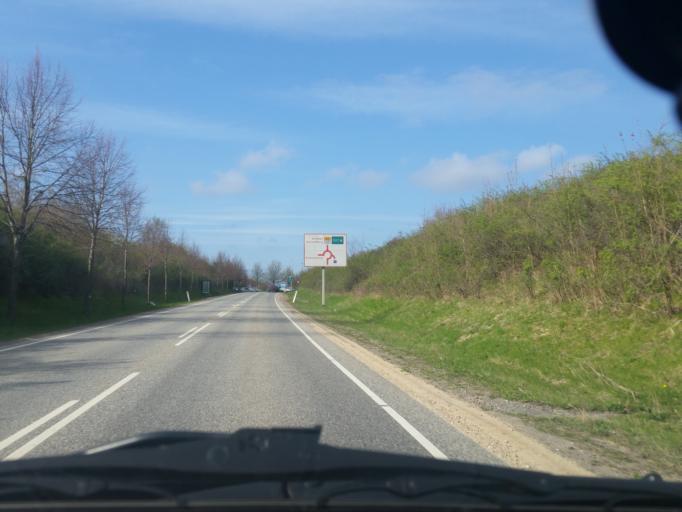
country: DK
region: Zealand
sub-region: Soro Kommune
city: Soro
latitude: 55.4537
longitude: 11.5617
